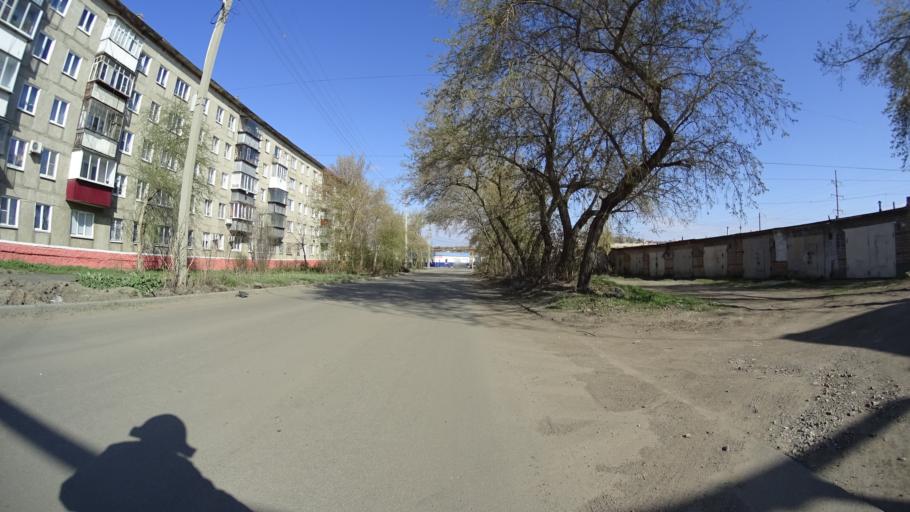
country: RU
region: Chelyabinsk
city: Troitsk
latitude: 54.0916
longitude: 61.5562
